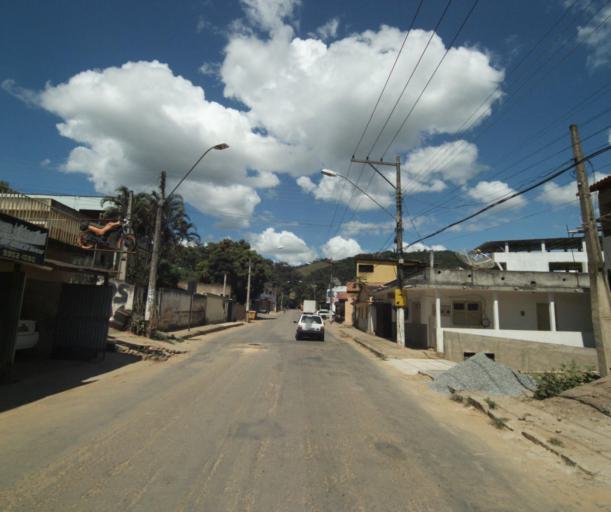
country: BR
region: Espirito Santo
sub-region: Mimoso Do Sul
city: Mimoso do Sul
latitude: -21.0717
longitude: -41.3558
